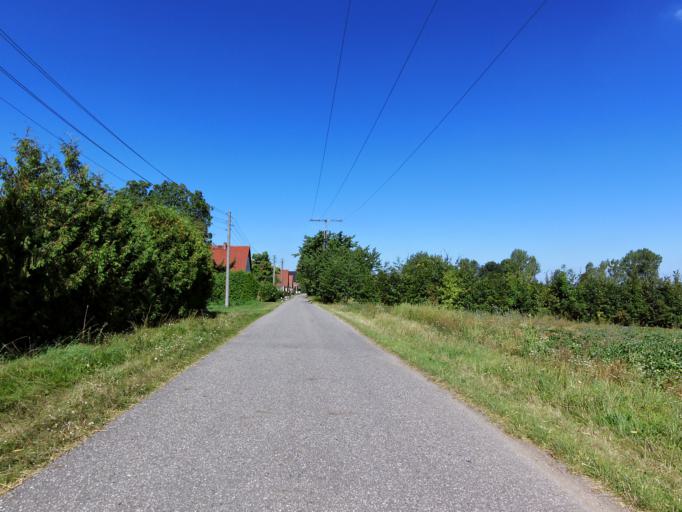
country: DE
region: Brandenburg
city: Muhlberg
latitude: 51.4063
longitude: 13.2219
